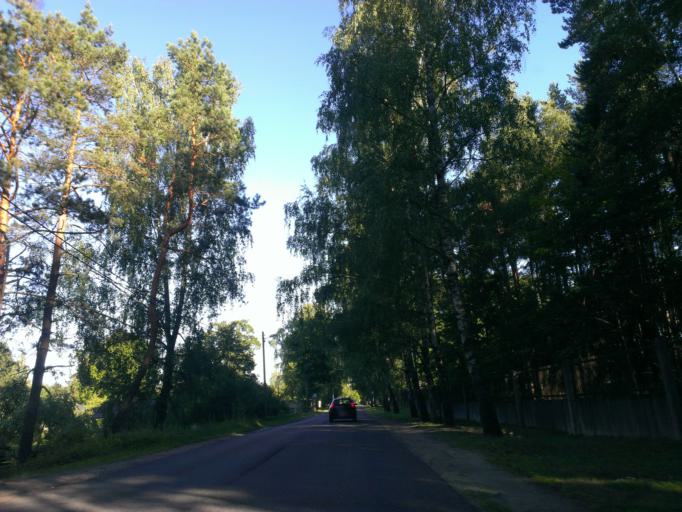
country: LV
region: Riga
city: Bergi
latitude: 56.9926
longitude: 24.2868
